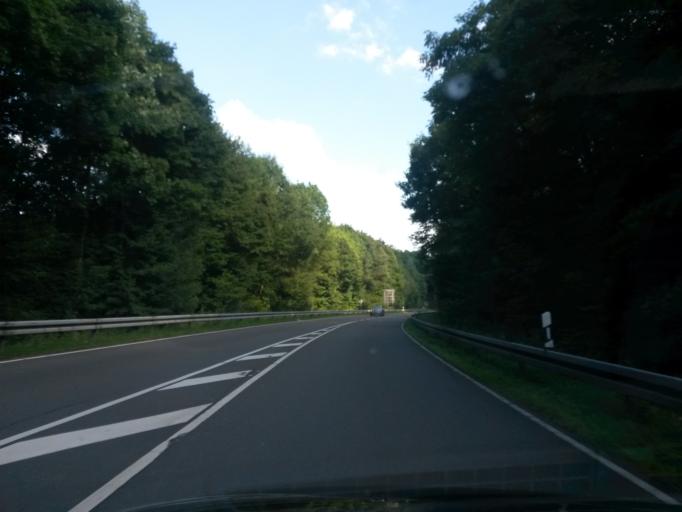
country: DE
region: North Rhine-Westphalia
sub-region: Regierungsbezirk Koln
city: Engelskirchen
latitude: 50.9746
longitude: 7.4690
